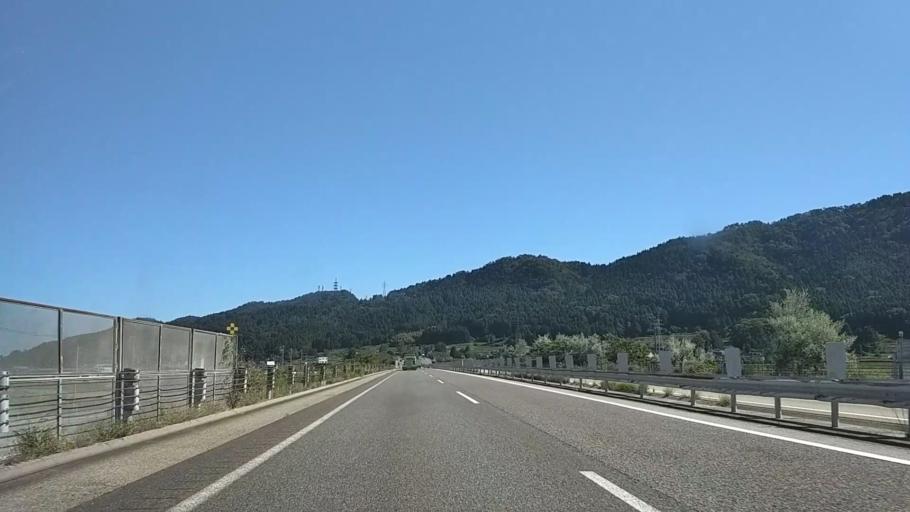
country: JP
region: Toyama
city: Nyuzen
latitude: 36.9468
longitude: 137.5631
